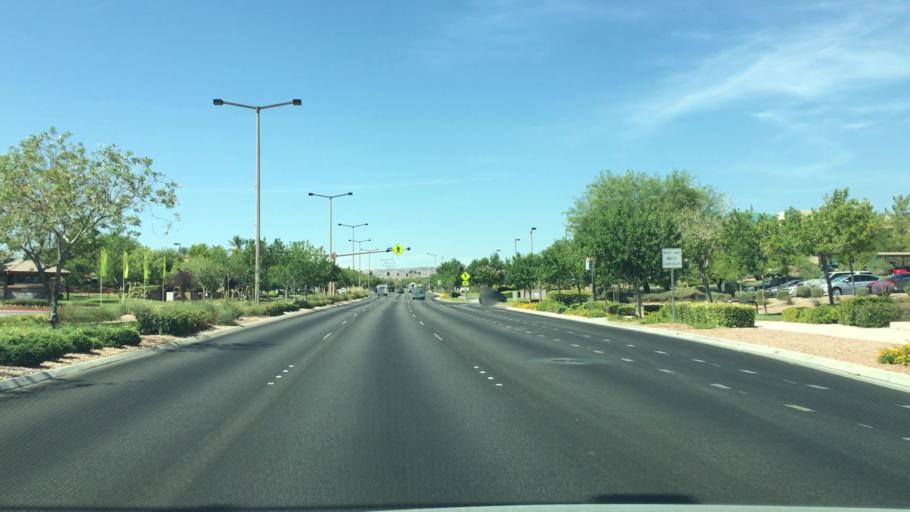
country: US
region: Nevada
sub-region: Clark County
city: Summerlin South
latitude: 36.1856
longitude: -115.3083
